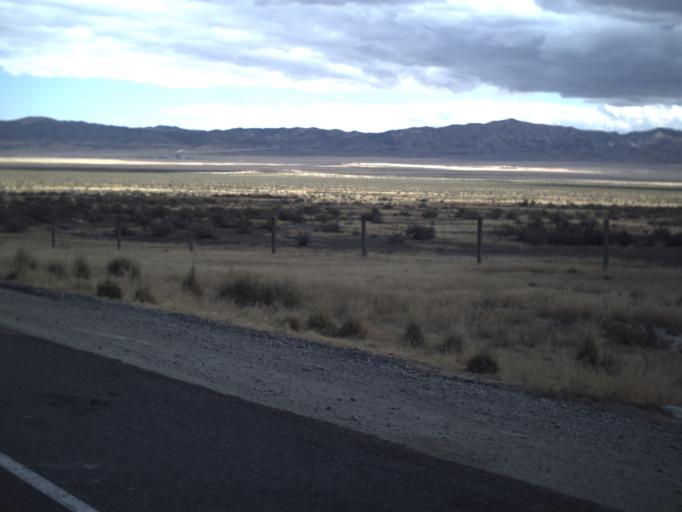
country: US
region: Utah
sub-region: Tooele County
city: Grantsville
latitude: 40.7304
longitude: -113.1131
